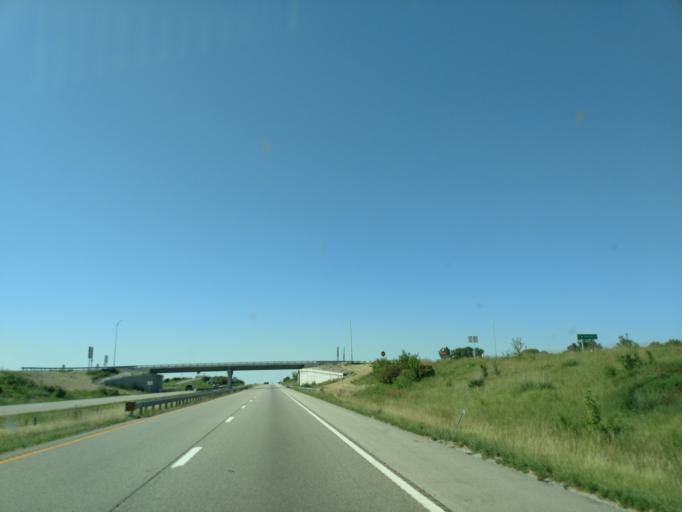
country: US
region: Kansas
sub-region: Doniphan County
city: Elwood
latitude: 39.5979
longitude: -94.7885
